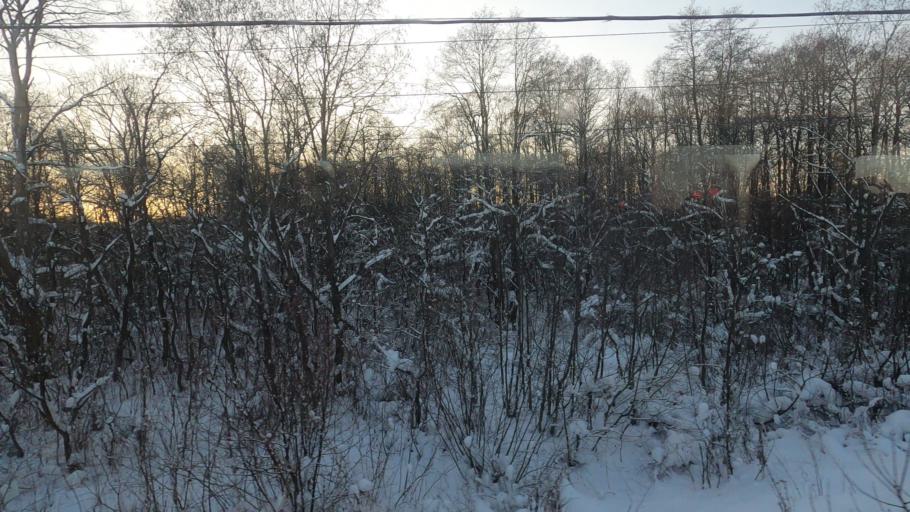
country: RU
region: Moskovskaya
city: Dmitrov
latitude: 56.3869
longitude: 37.5114
